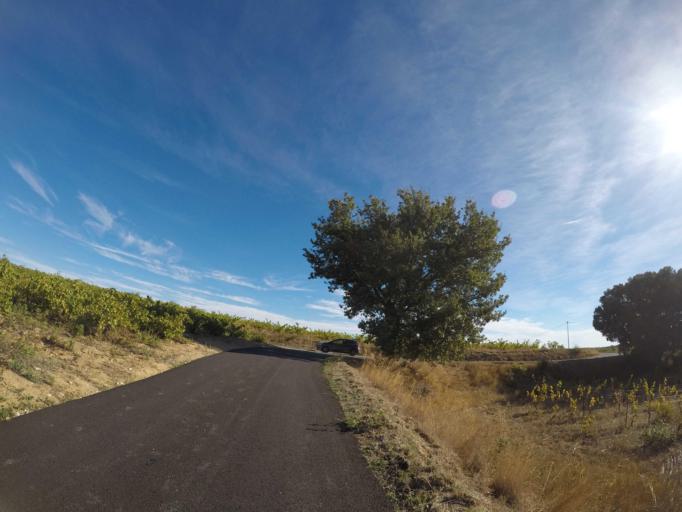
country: FR
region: Languedoc-Roussillon
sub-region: Departement des Pyrenees-Orientales
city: Trouillas
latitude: 42.5698
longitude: 2.7951
